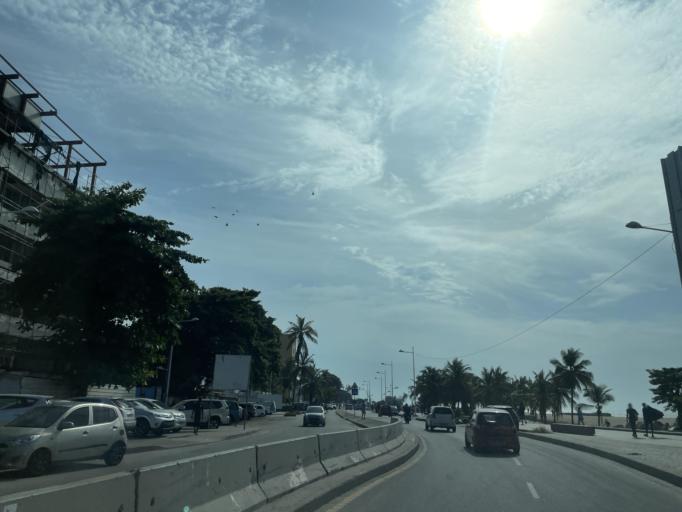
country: AO
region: Luanda
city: Luanda
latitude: -8.7787
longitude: 13.2421
